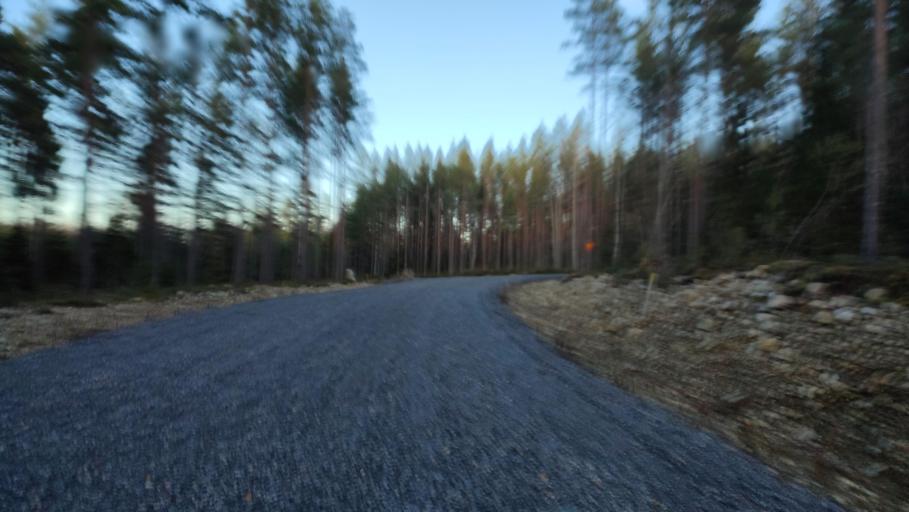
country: FI
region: Southern Ostrobothnia
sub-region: Suupohja
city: Karijoki
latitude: 62.2852
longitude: 21.6310
